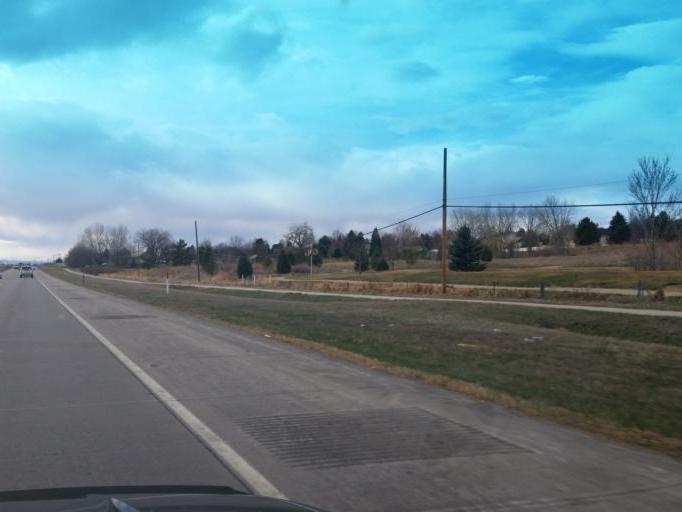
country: US
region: Colorado
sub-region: Weld County
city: Greeley
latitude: 40.3922
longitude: -104.7710
